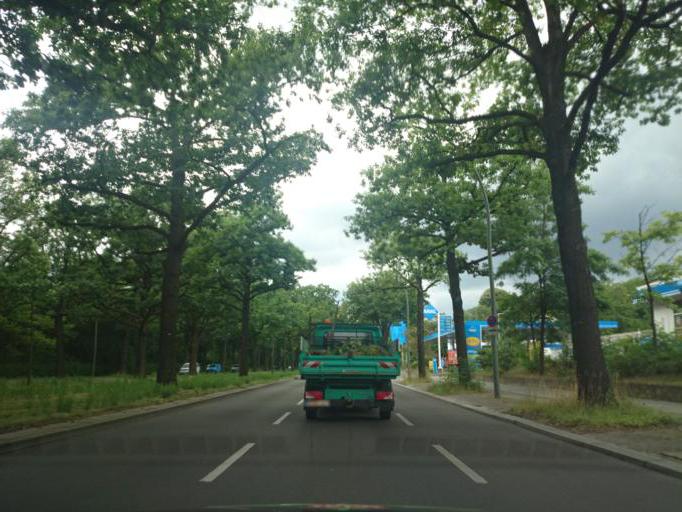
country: DE
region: Berlin
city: Zehlendorf Bezirk
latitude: 52.4332
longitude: 13.2391
